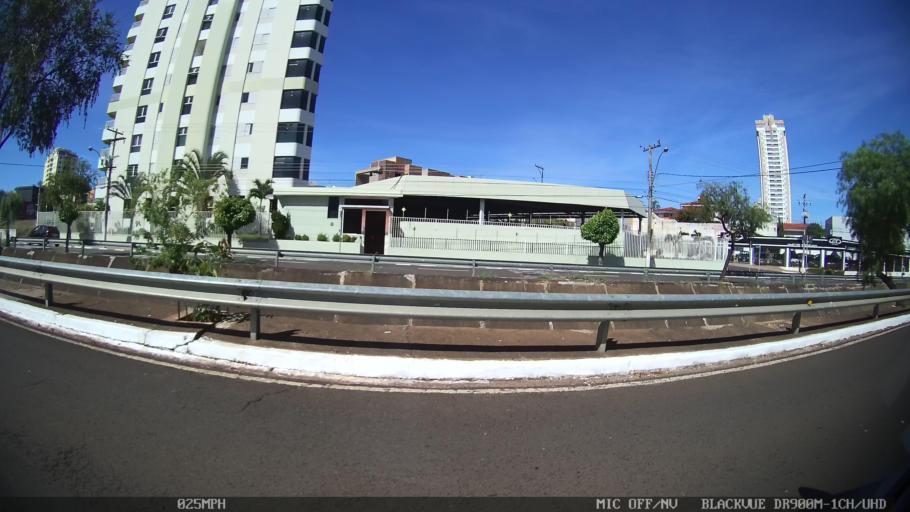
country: BR
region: Sao Paulo
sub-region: Franca
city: Franca
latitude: -20.5389
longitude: -47.3925
